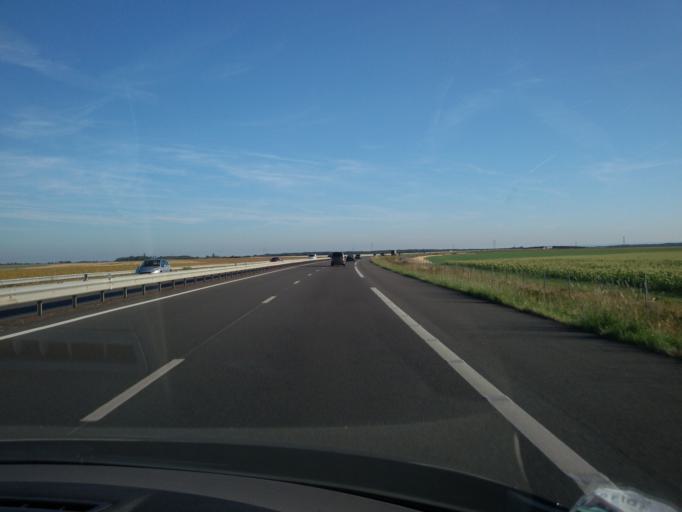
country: FR
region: Centre
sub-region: Departement du Cher
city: Levet
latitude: 46.9473
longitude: 2.4165
